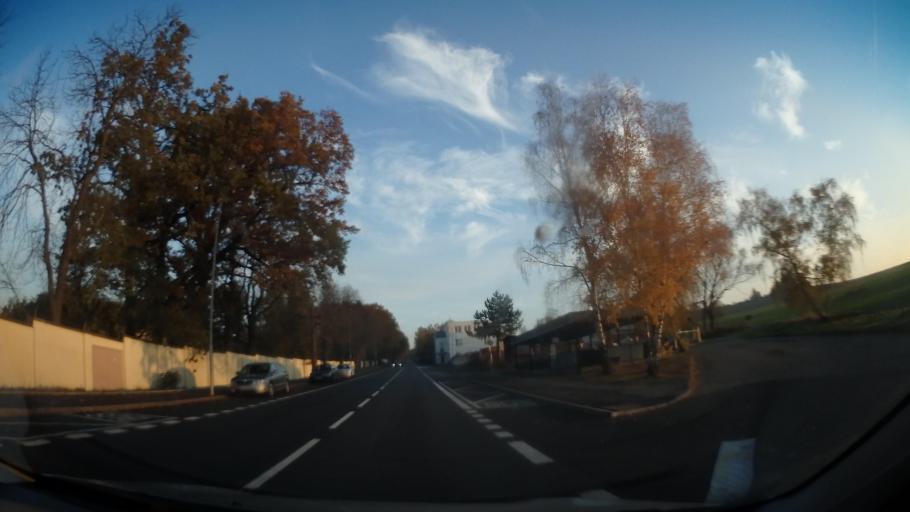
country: CZ
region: Central Bohemia
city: Vlasim
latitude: 49.6938
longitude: 14.9098
